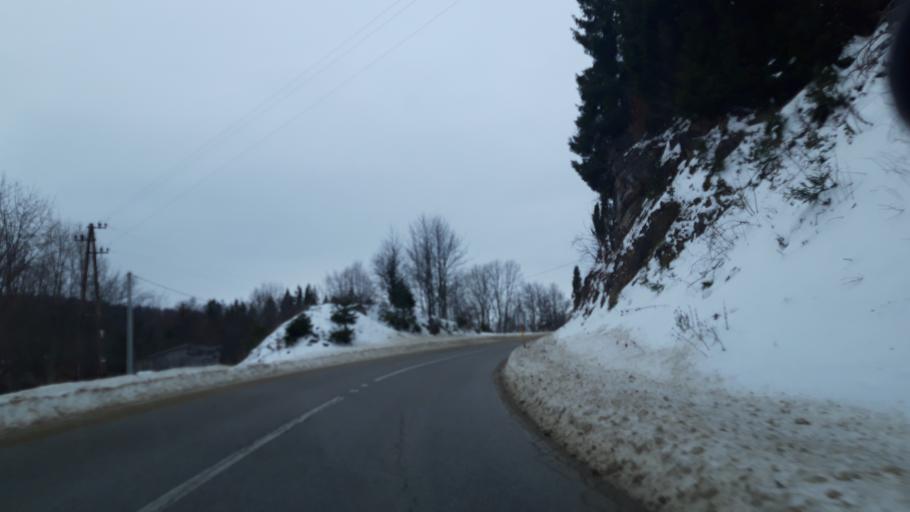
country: BA
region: Republika Srpska
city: Vlasenica
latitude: 44.1450
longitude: 18.9436
